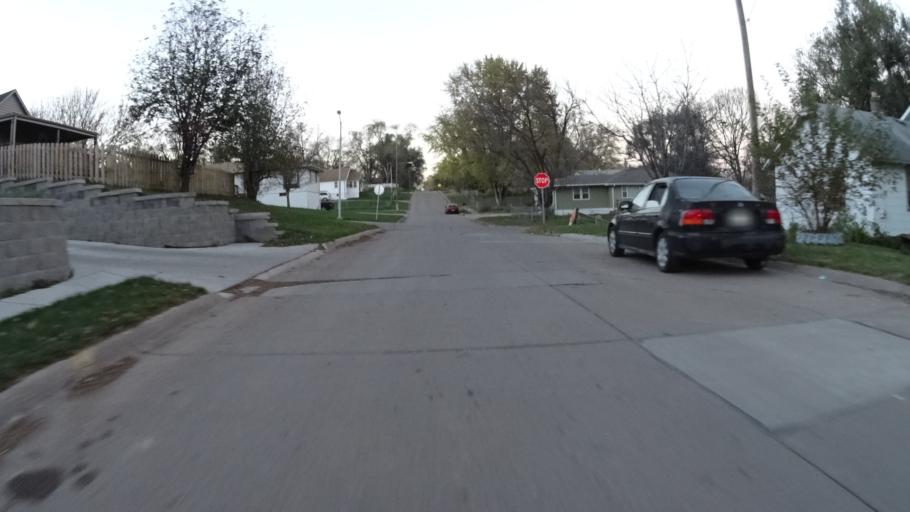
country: US
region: Nebraska
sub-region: Douglas County
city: Omaha
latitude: 41.1915
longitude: -95.9505
